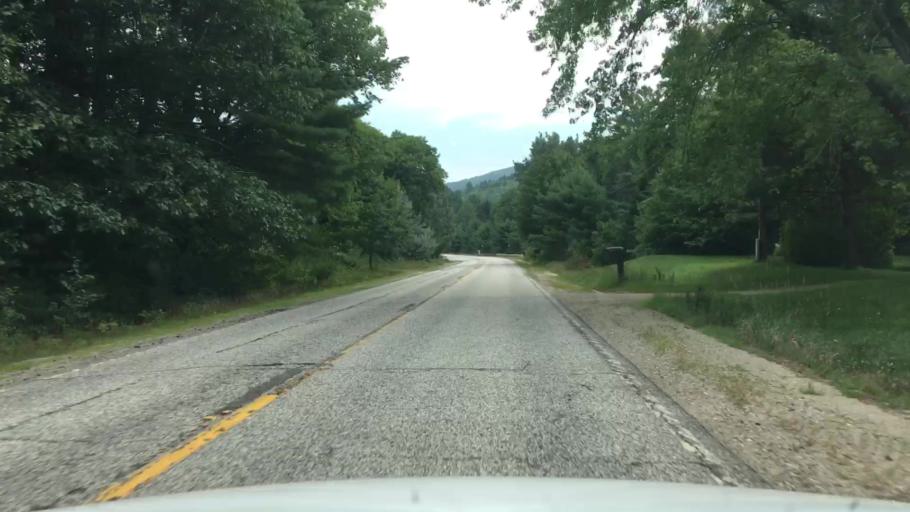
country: US
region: Maine
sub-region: Oxford County
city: Rumford
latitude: 44.5831
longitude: -70.7340
